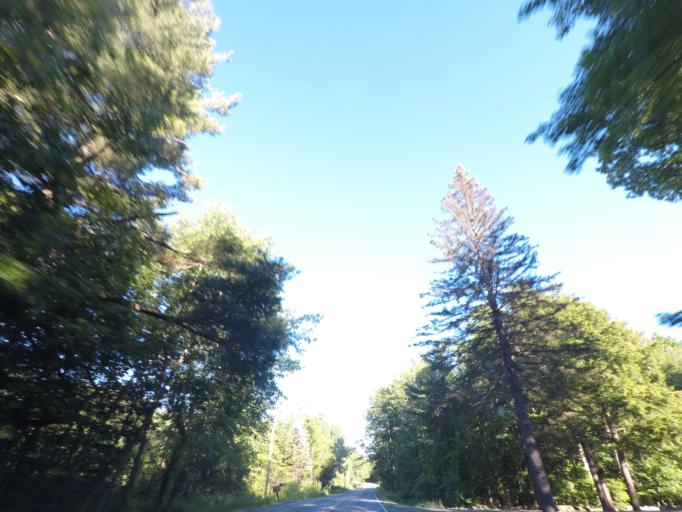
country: US
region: New York
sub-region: Rensselaer County
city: West Sand Lake
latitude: 42.5965
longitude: -73.5941
